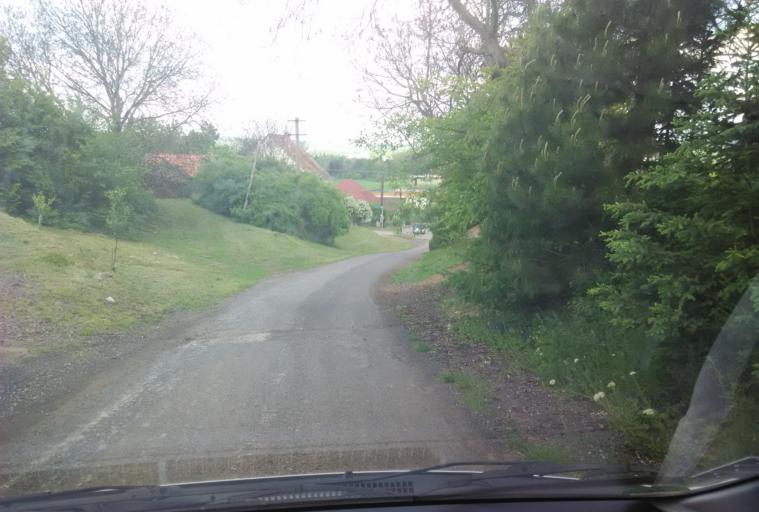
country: SK
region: Banskobystricky
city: Dudince
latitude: 48.1649
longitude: 18.8966
